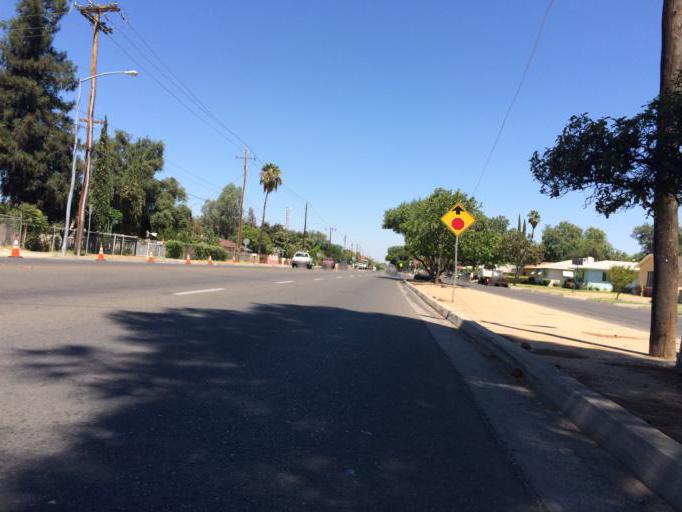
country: US
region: California
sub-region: Fresno County
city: Fresno
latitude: 36.7219
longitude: -119.7456
